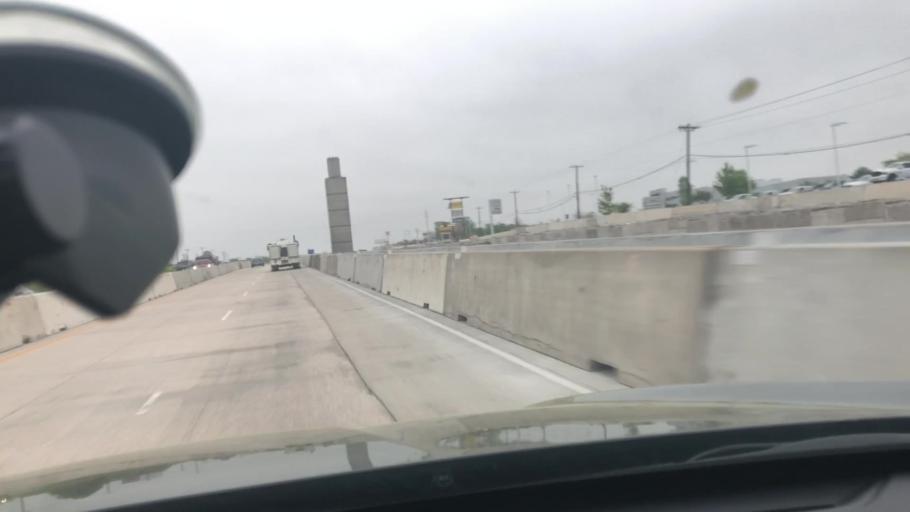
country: US
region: Texas
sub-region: Bell County
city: Temple
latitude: 31.0924
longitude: -97.3818
